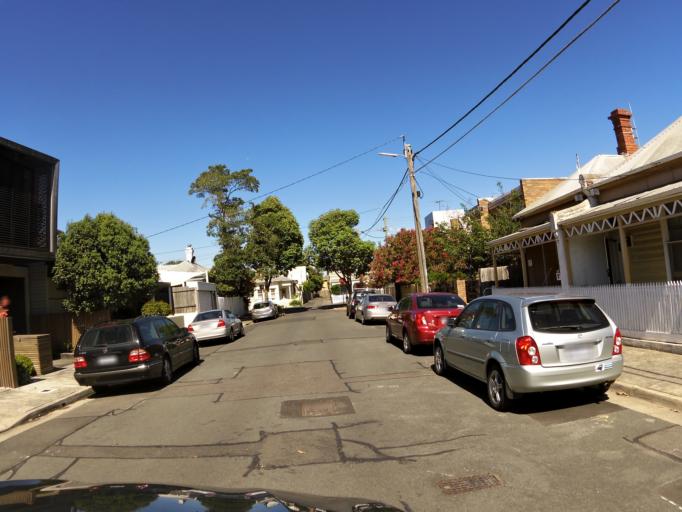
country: AU
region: Victoria
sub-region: Yarra
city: Richmond
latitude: -37.8135
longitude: 145.0026
